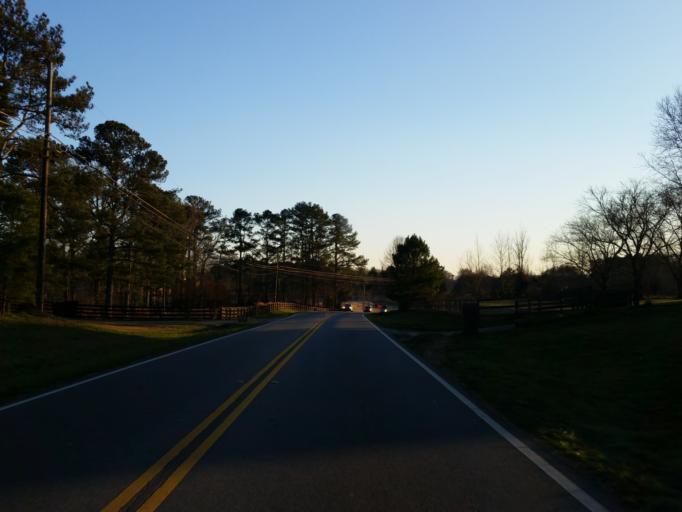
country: US
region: Georgia
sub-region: Cherokee County
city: Holly Springs
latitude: 34.1654
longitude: -84.4244
